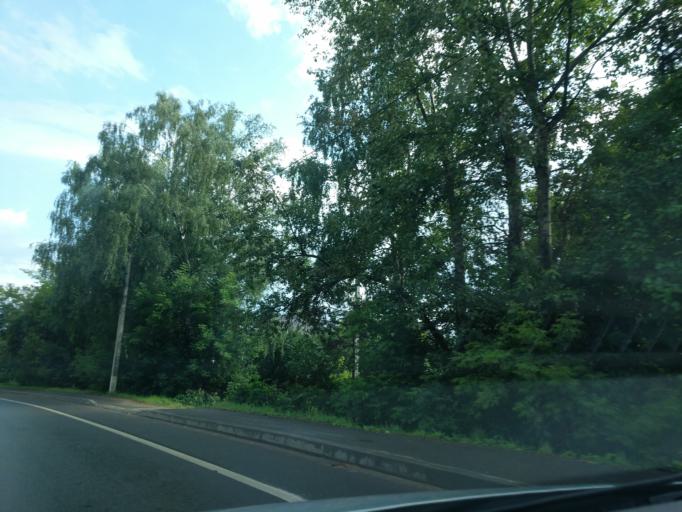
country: RU
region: Moskovskaya
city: Lobnya
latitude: 56.0114
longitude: 37.5054
